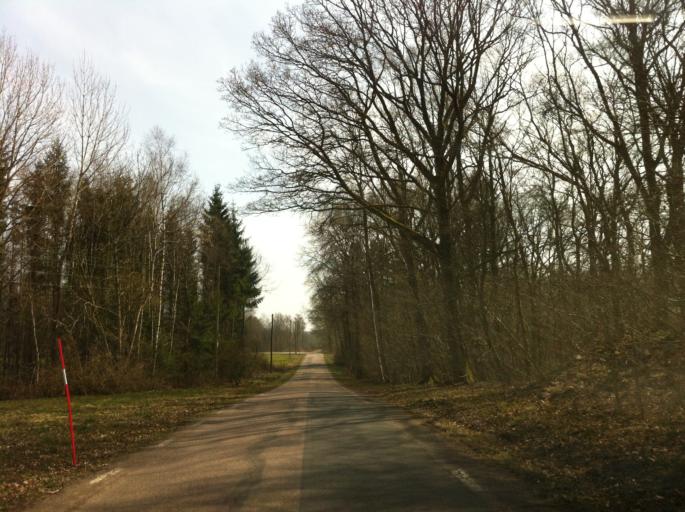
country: SE
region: Skane
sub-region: Klippans Kommun
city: Ljungbyhed
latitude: 55.9934
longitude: 13.2338
